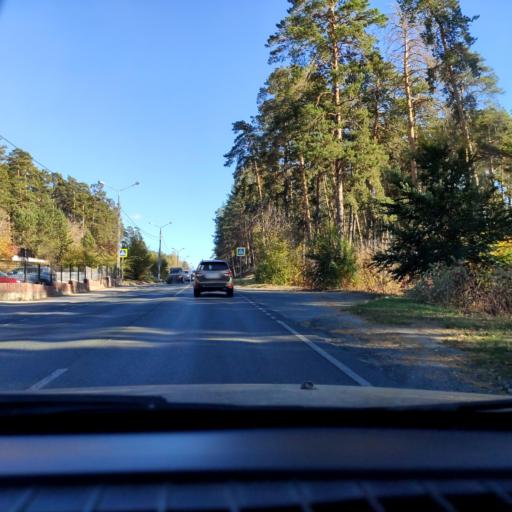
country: RU
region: Samara
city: Tol'yatti
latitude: 53.4760
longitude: 49.3346
